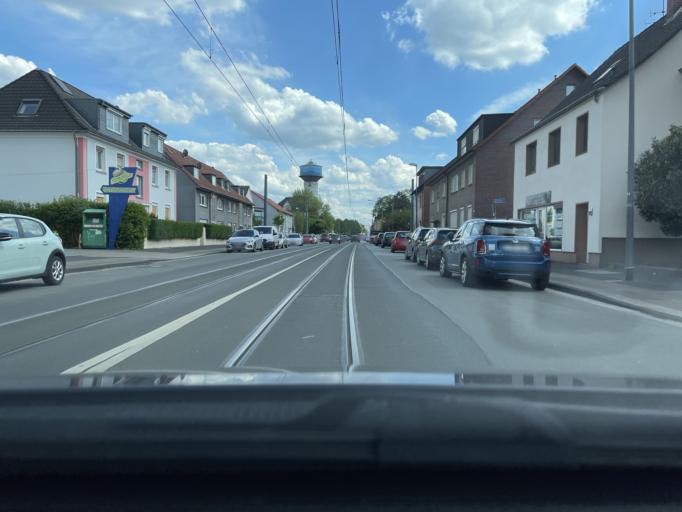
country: DE
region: North Rhine-Westphalia
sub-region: Regierungsbezirk Dusseldorf
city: Oberhausen
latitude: 51.4725
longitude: 6.9178
